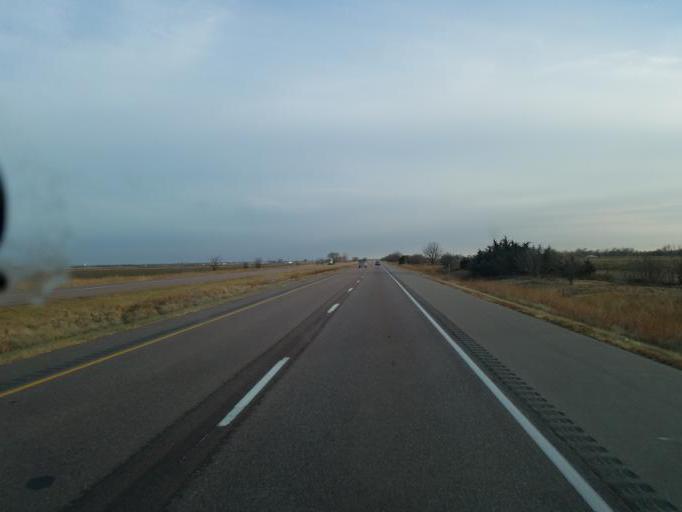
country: US
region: Iowa
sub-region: Monona County
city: Onawa
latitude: 42.0607
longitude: -96.1603
